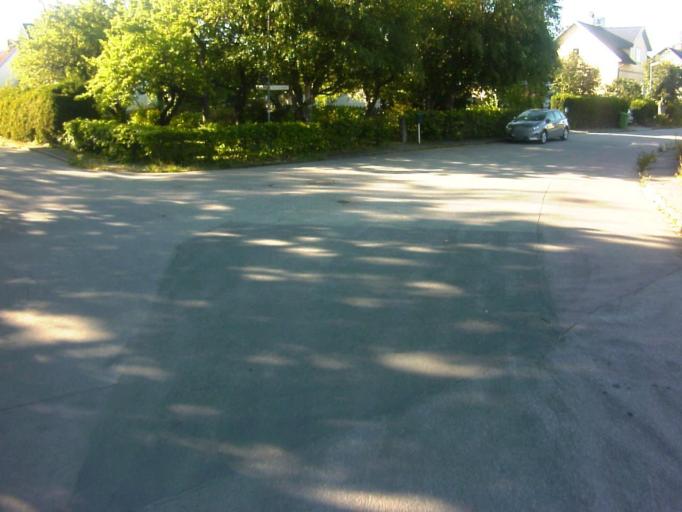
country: SE
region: Soedermanland
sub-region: Eskilstuna Kommun
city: Eskilstuna
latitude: 59.3818
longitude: 16.5369
